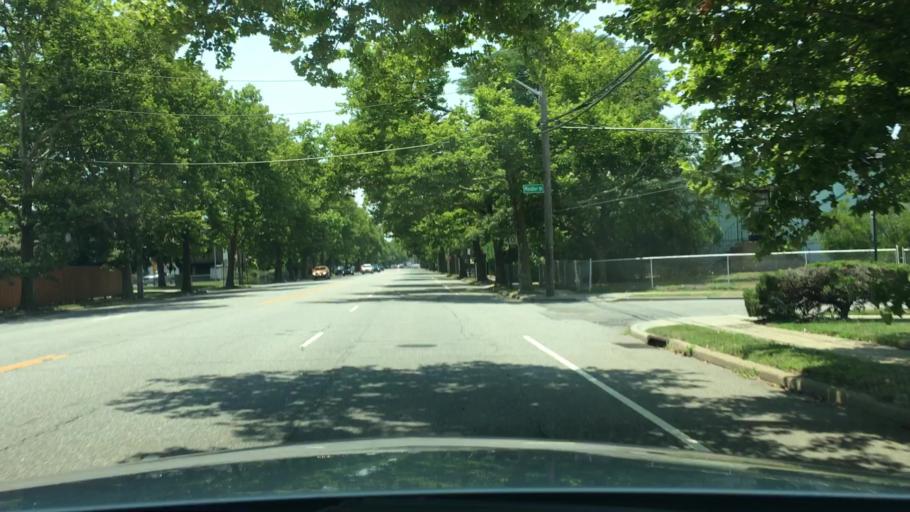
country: US
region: New York
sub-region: Nassau County
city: Hicksville
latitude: 40.7756
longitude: -73.5127
